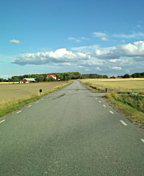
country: SE
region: Uppsala
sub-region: Enkopings Kommun
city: Grillby
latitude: 59.6845
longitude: 17.2119
